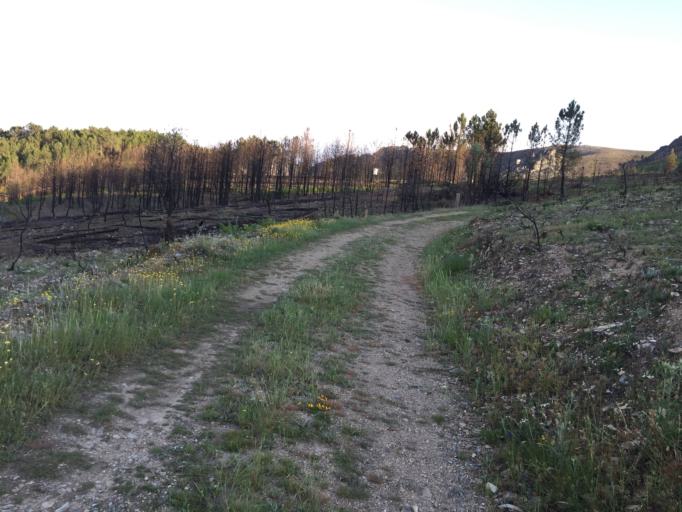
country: PT
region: Coimbra
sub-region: Pampilhosa da Serra
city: Pampilhosa da Serra
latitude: 40.1105
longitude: -7.8731
